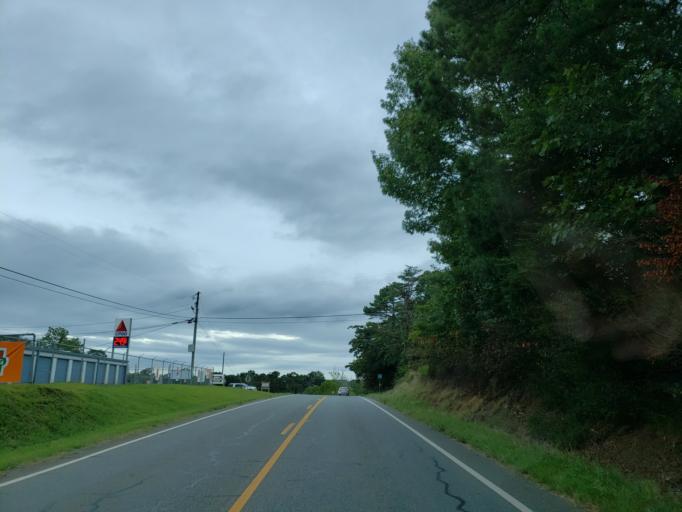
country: US
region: Georgia
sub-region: Gilmer County
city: Ellijay
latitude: 34.6391
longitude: -84.5214
